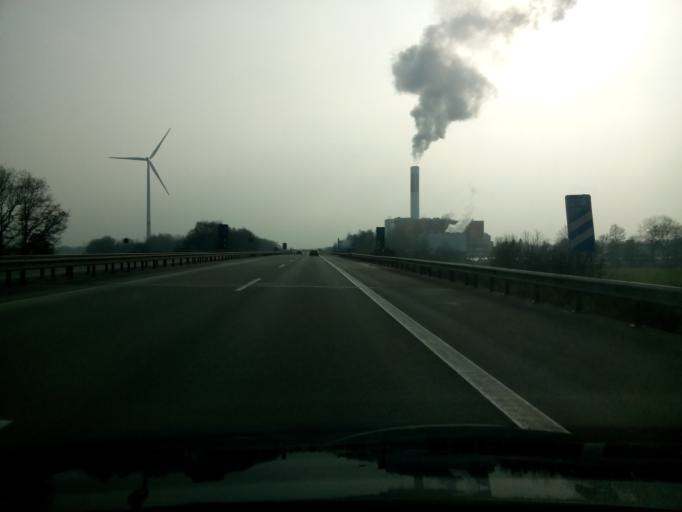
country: DE
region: Lower Saxony
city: Schiffdorf
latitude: 53.5527
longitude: 8.6194
